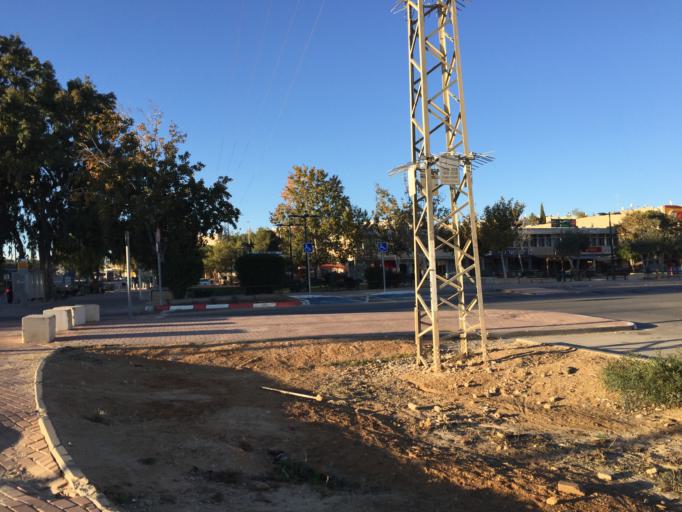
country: IL
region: Southern District
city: Mitzpe Ramon
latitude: 30.6129
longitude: 34.8036
